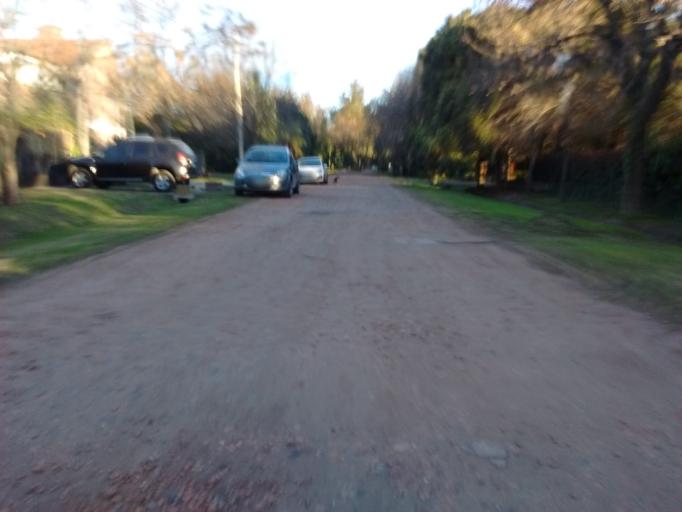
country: AR
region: Santa Fe
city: Funes
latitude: -32.9147
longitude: -60.8329
